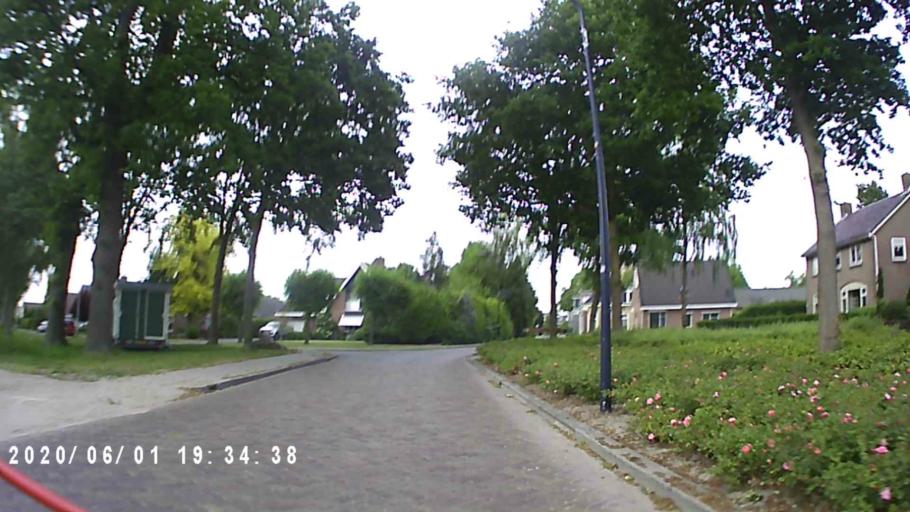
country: NL
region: Friesland
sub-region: Gemeente Achtkarspelen
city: Augustinusga
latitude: 53.2172
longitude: 6.1603
